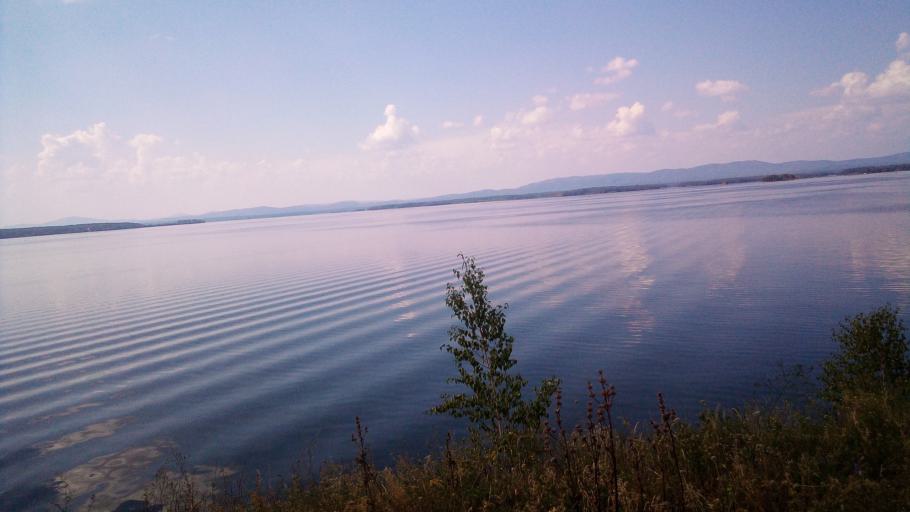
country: RU
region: Chelyabinsk
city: Ozersk
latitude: 55.7873
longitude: 60.7443
